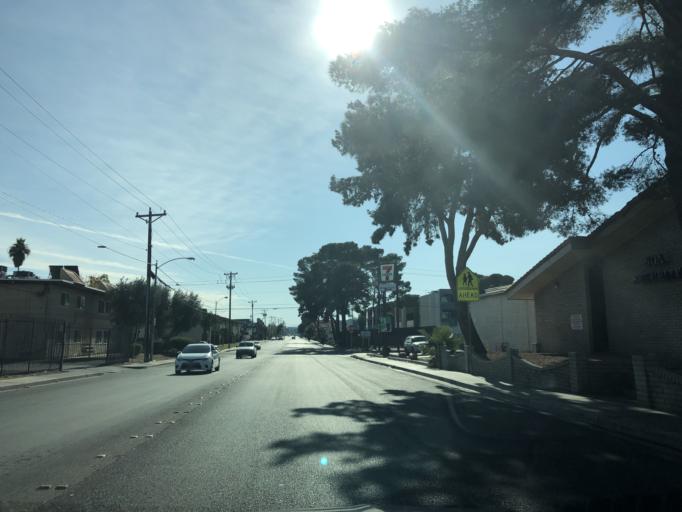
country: US
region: Nevada
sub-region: Clark County
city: Winchester
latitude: 36.1277
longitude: -115.1416
